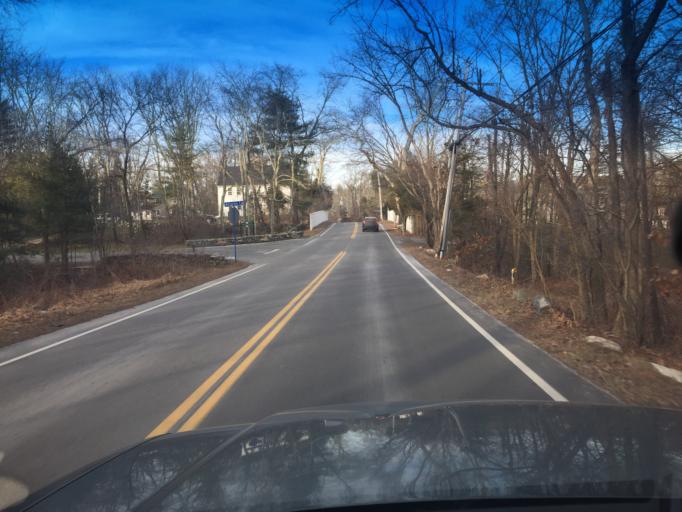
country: US
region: Massachusetts
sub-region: Middlesex County
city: Holliston
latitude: 42.1766
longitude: -71.4115
